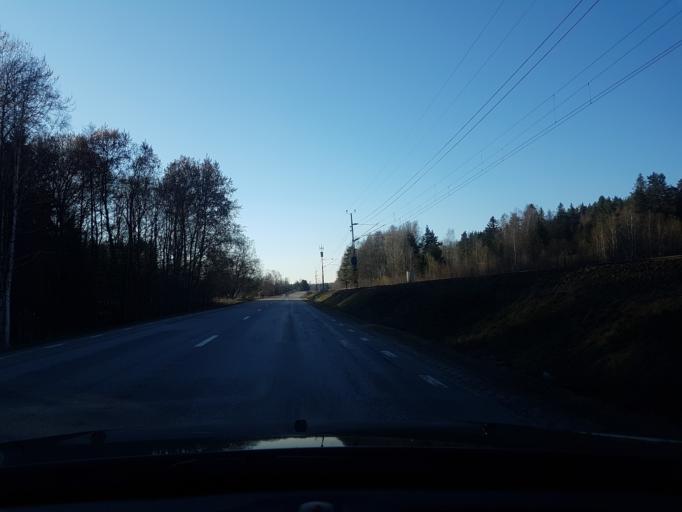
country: SE
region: Uppsala
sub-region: Heby Kommun
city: Morgongava
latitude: 59.9239
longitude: 16.9864
